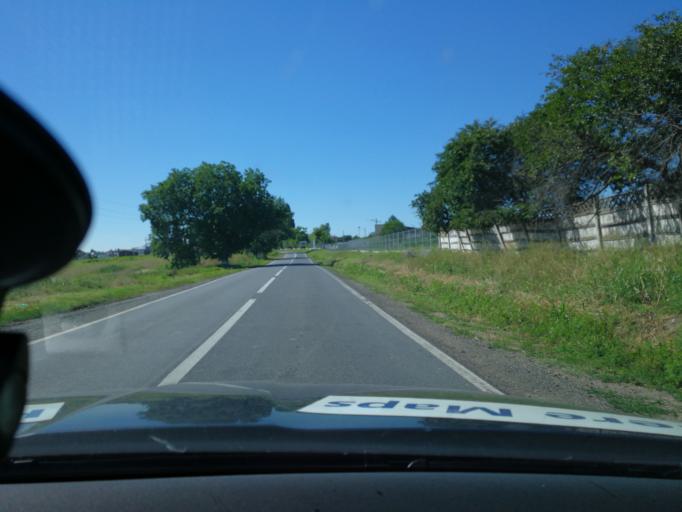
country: RO
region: Tulcea
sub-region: Oras Macin
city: Macin
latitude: 45.2377
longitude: 28.1542
